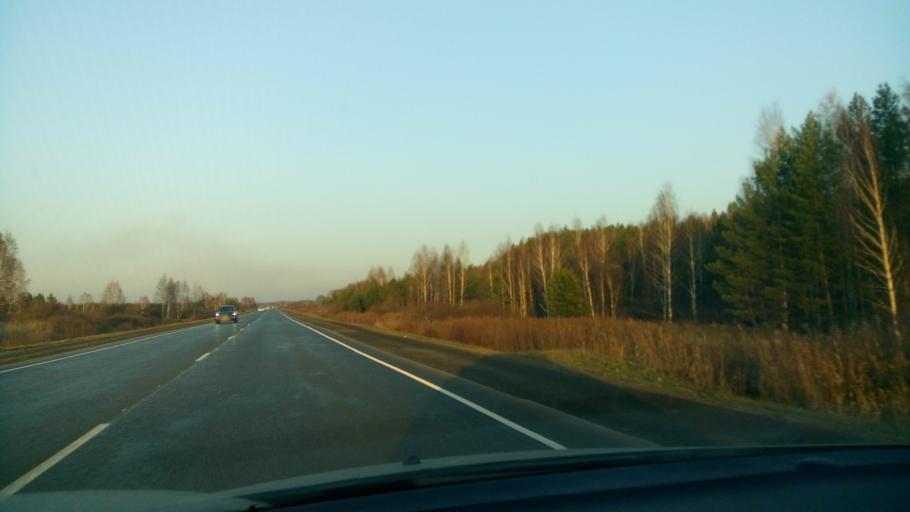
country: RU
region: Sverdlovsk
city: Obukhovskoye
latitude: 56.8262
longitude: 62.5573
